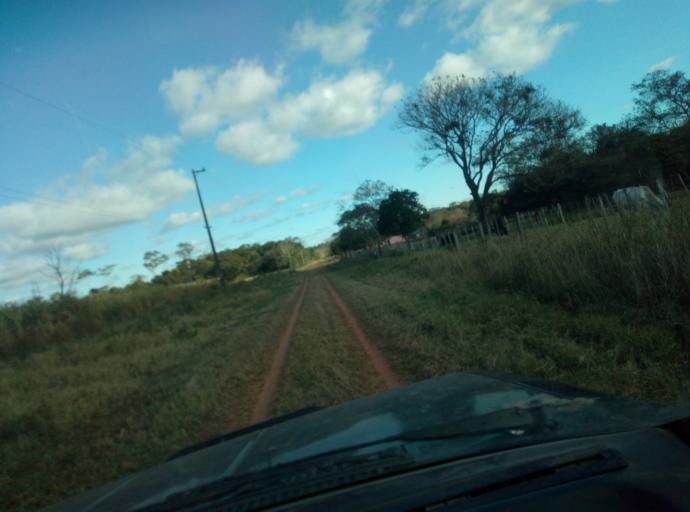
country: PY
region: Caaguazu
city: Doctor Cecilio Baez
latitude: -25.1672
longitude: -56.2727
